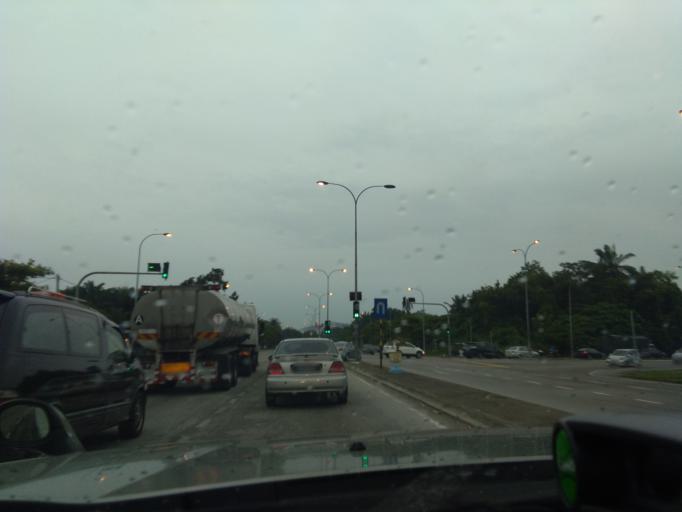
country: MY
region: Penang
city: Nibong Tebal
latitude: 5.1867
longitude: 100.4874
